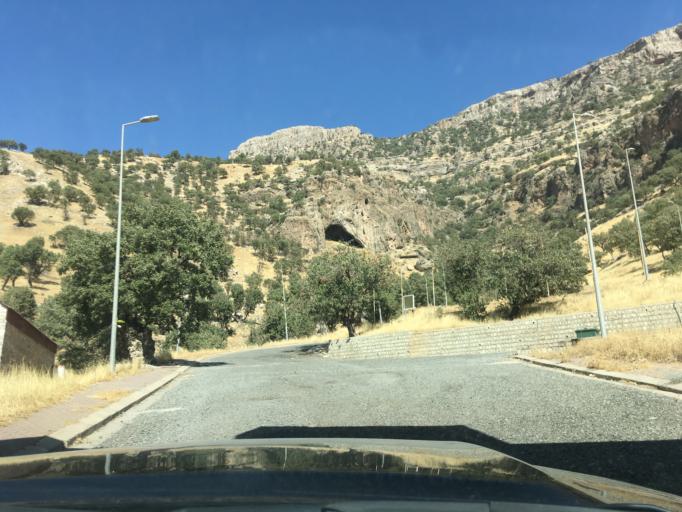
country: IQ
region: Arbil
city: Mergasur
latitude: 36.8323
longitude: 44.2175
